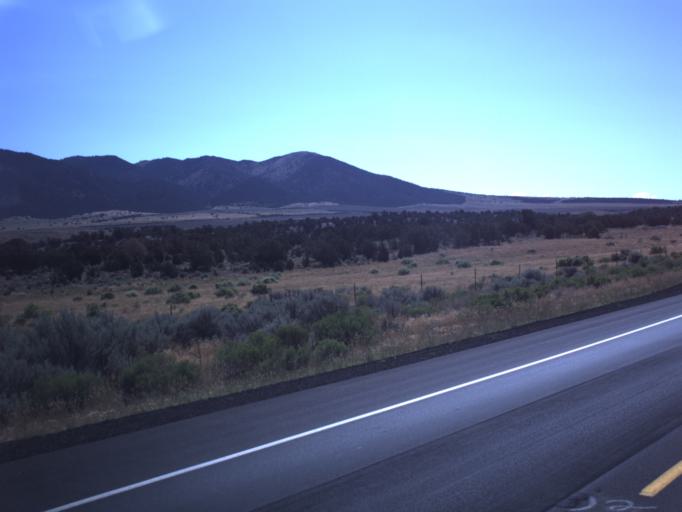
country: US
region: Utah
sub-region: Utah County
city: Eagle Mountain
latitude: 40.0271
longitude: -112.2825
